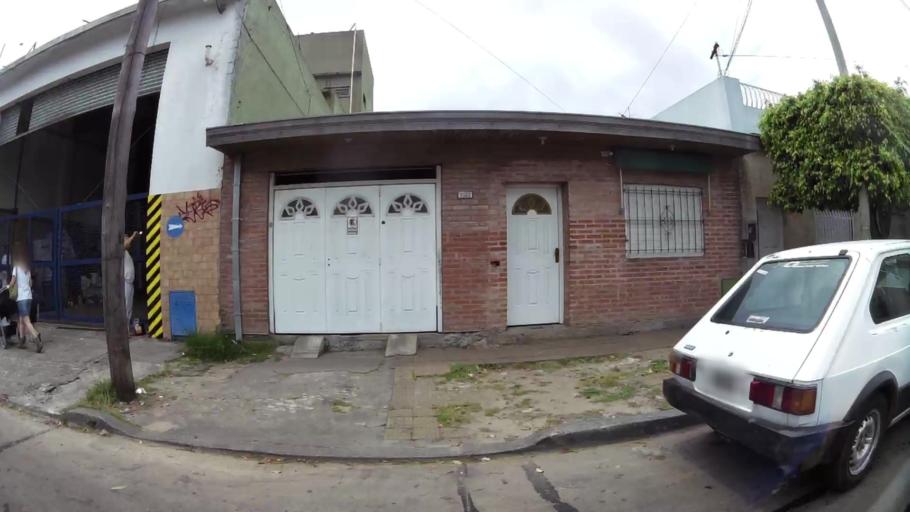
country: AR
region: Buenos Aires
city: San Justo
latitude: -34.6654
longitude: -58.5332
